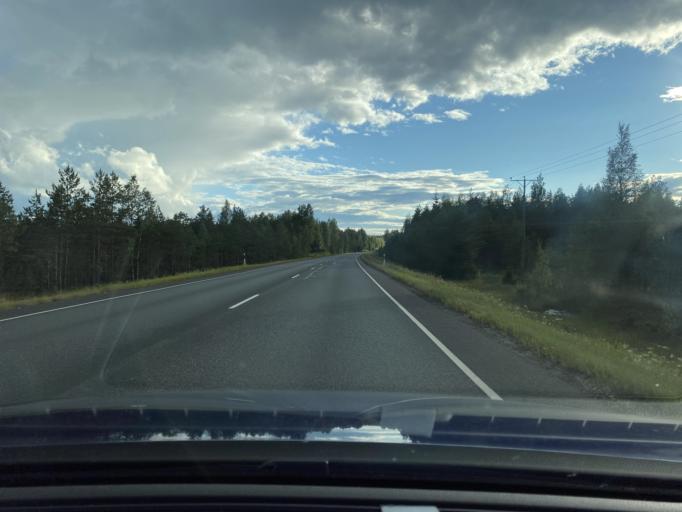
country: FI
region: Haeme
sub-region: Haemeenlinna
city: Renko
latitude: 60.8326
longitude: 24.0599
